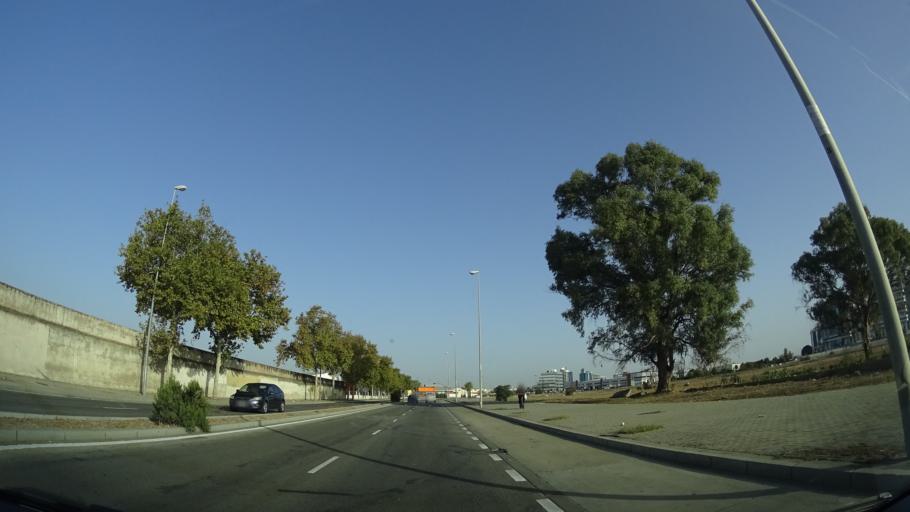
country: ES
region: Andalusia
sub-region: Provincia de Sevilla
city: Sevilla
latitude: 37.4218
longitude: -5.9773
